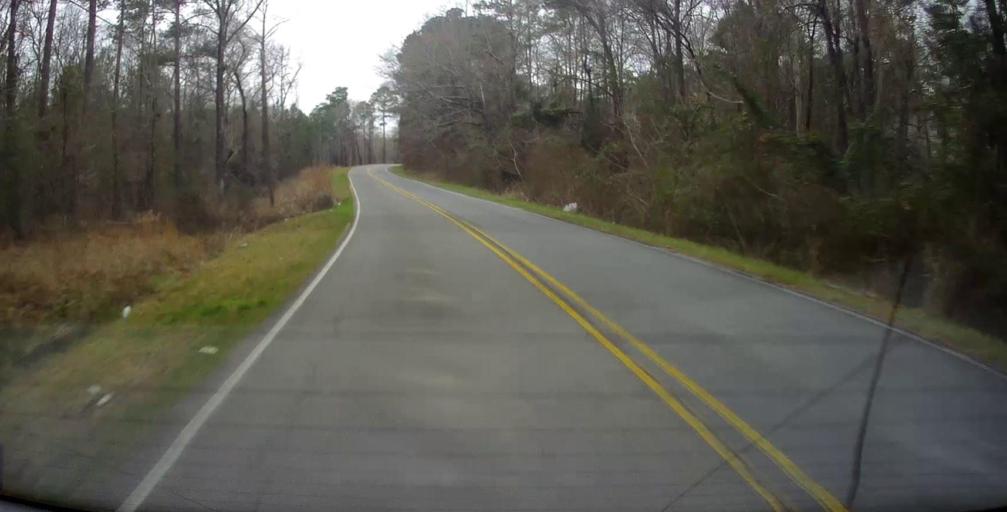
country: US
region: Georgia
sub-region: Bibb County
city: Macon
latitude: 32.8589
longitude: -83.7074
